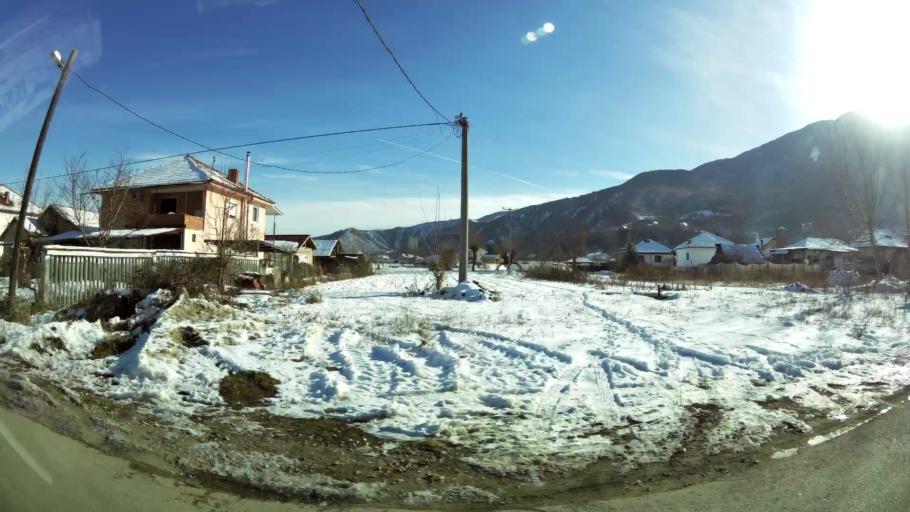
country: MK
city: Grchec
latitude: 41.9767
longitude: 21.3091
